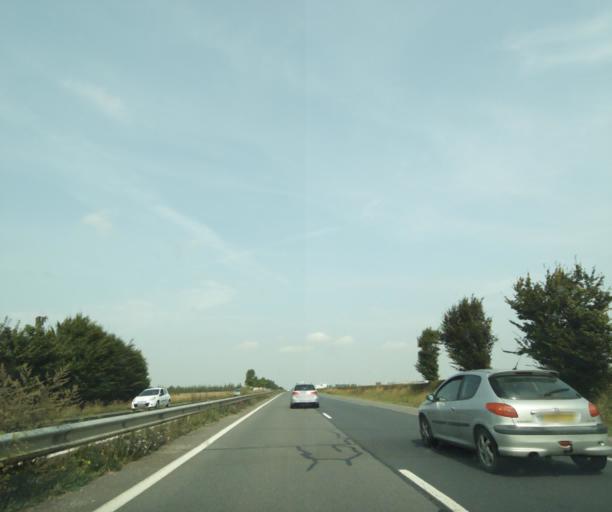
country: FR
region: Lower Normandy
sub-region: Departement du Calvados
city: Bretteville-sur-Laize
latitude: 49.0609
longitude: -0.2901
